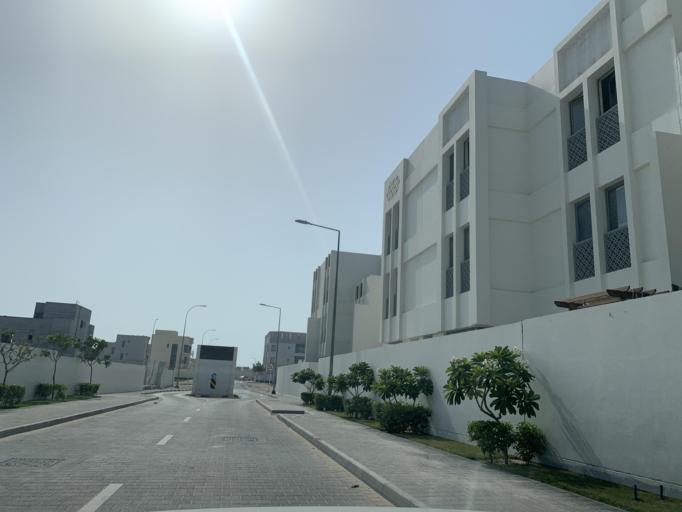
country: BH
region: Muharraq
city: Al Muharraq
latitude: 26.3101
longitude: 50.6363
